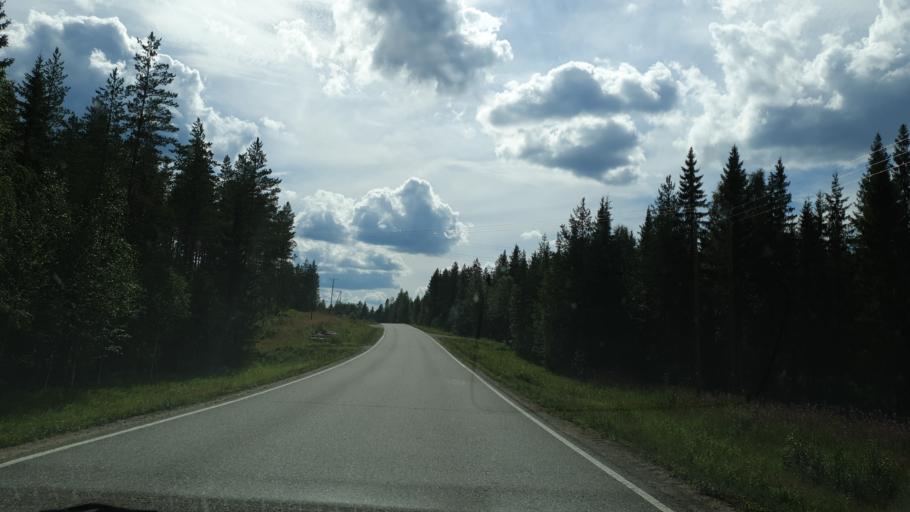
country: FI
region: Kainuu
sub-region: Kajaani
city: Sotkamo
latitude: 64.1980
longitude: 28.4647
